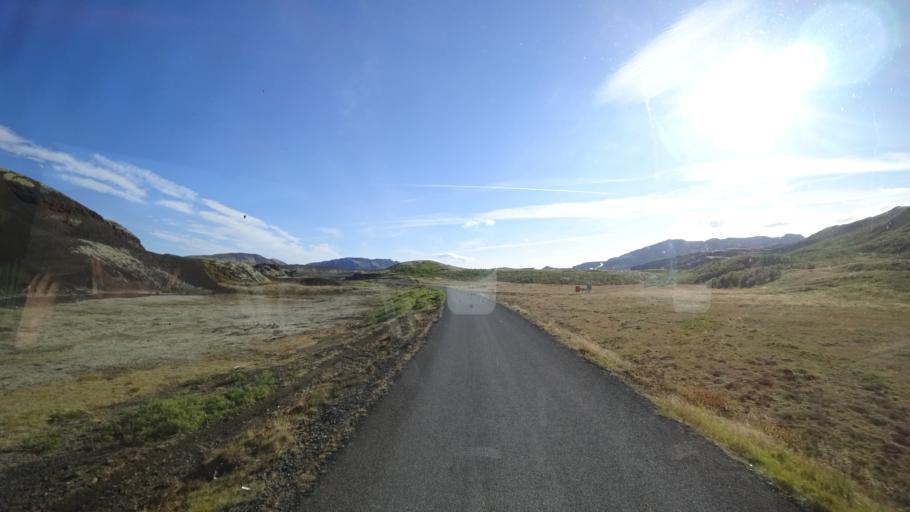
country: IS
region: South
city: Hveragerdi
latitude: 64.1262
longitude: -21.2499
